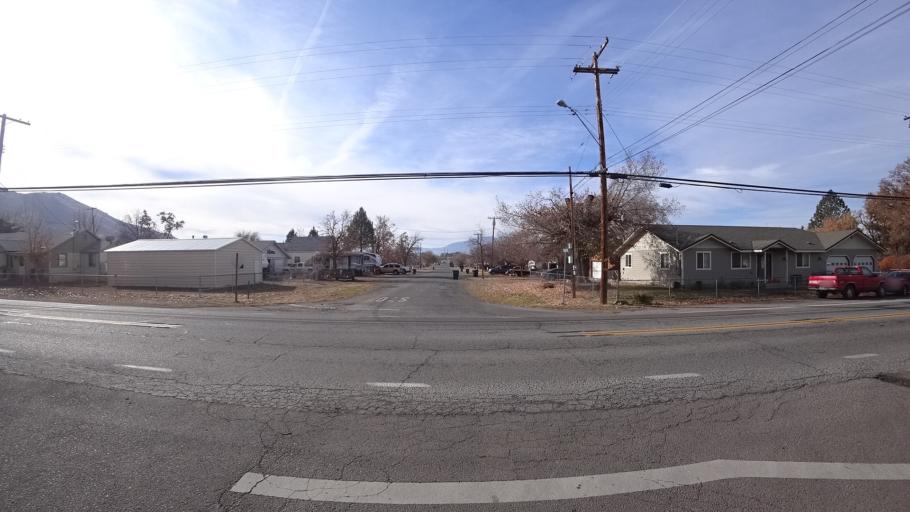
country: US
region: California
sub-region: Siskiyou County
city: Montague
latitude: 41.7266
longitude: -122.5234
